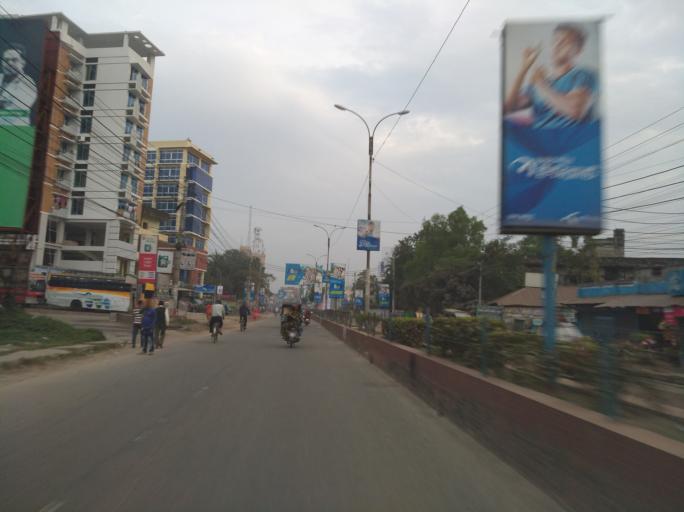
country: BD
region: Khulna
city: Khulna
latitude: 22.8259
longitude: 89.5508
